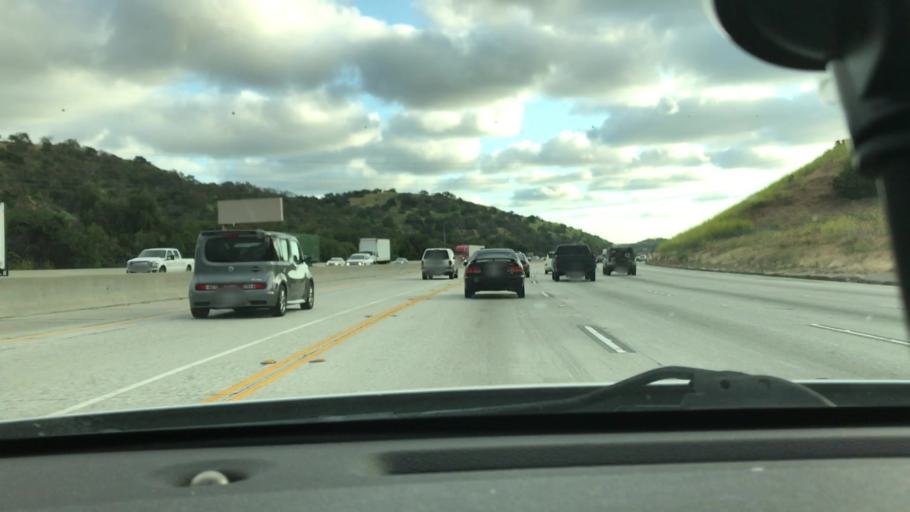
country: US
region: California
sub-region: Los Angeles County
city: Rowland Heights
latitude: 33.9632
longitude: -117.8527
